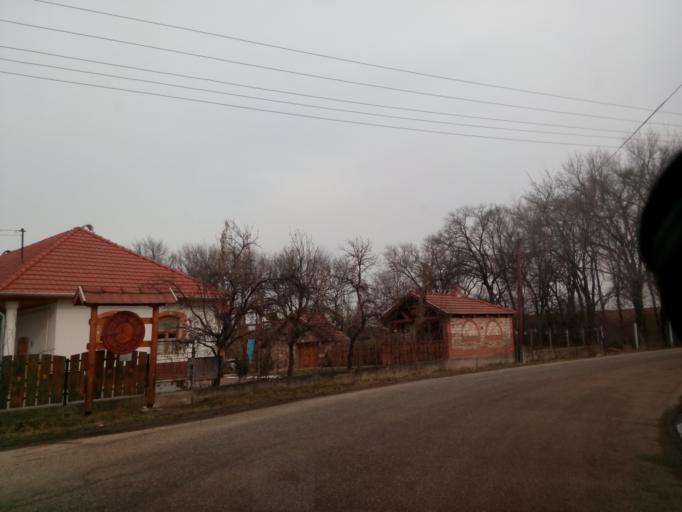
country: HU
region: Borsod-Abauj-Zemplen
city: Gonc
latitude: 48.4765
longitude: 21.2815
